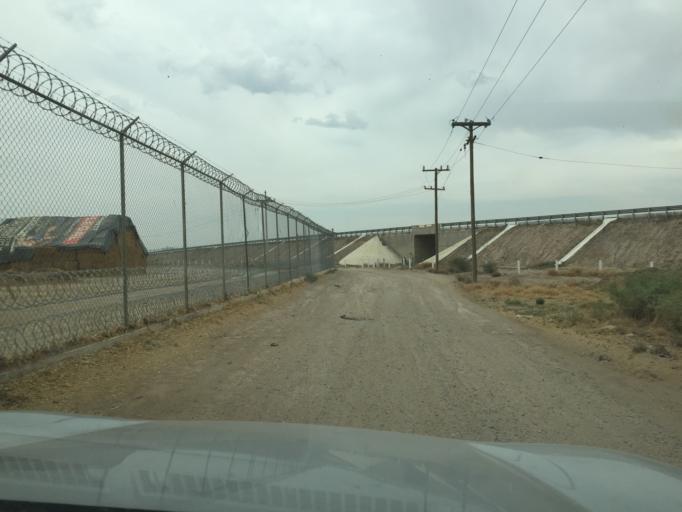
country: MX
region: Durango
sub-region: Gomez Palacio
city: San Jose de Vinedo
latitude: 25.6553
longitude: -103.4423
